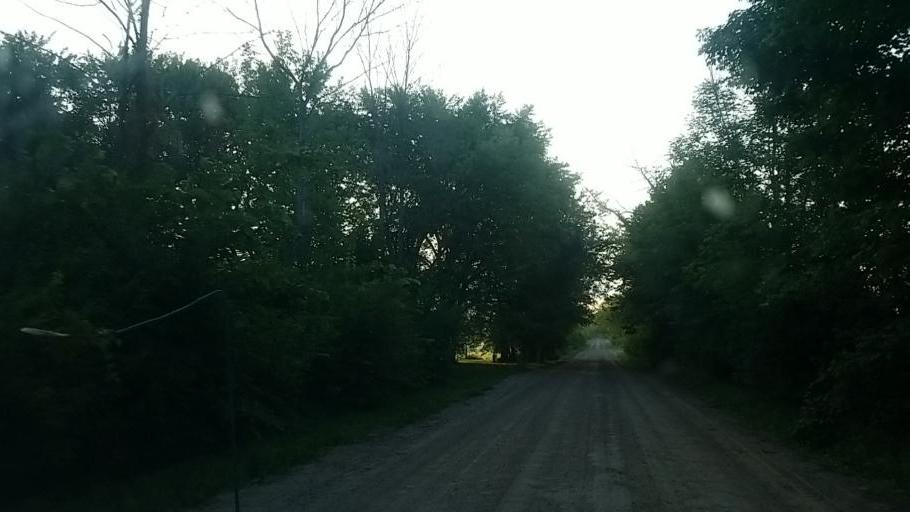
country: US
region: Michigan
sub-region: Osceola County
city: Evart
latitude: 43.9152
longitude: -85.1979
